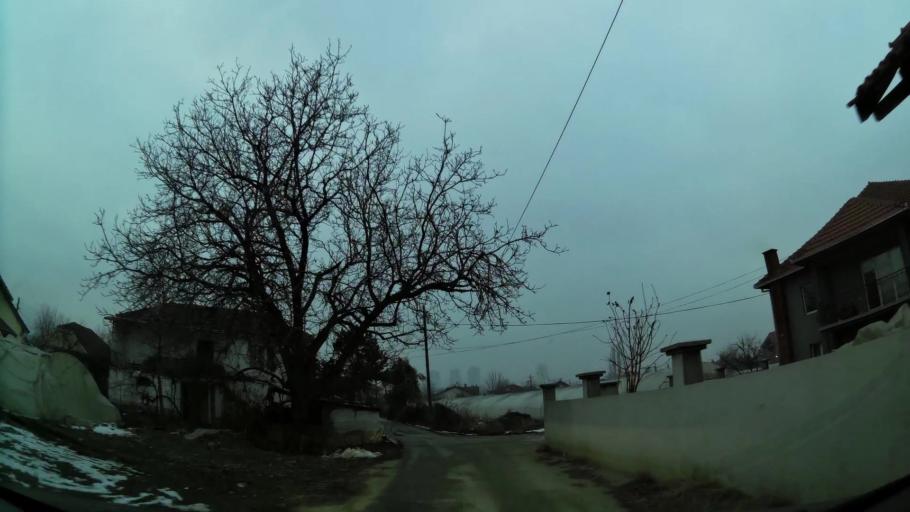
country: MK
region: Kisela Voda
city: Usje
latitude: 41.9689
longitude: 21.4771
